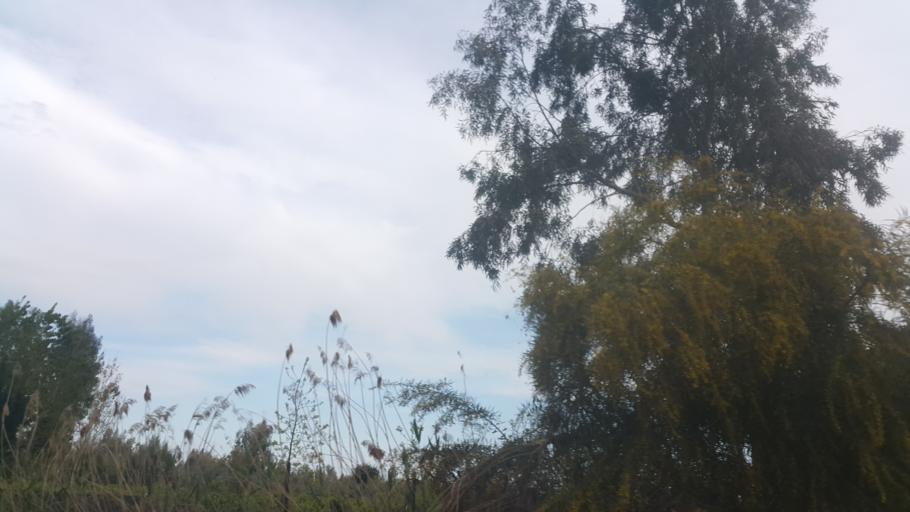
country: TR
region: Mersin
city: Yenice
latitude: 36.9488
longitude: 34.9891
